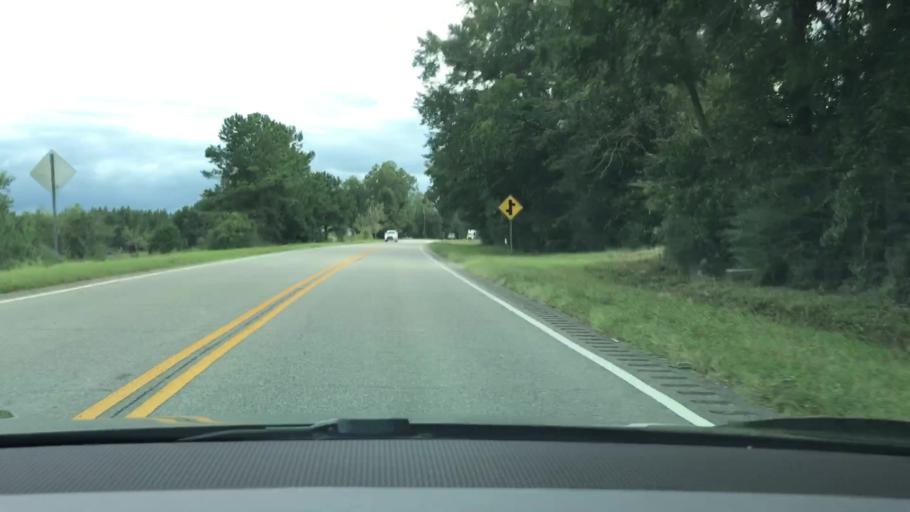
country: US
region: Alabama
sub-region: Coffee County
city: Elba
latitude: 31.5561
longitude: -86.0142
